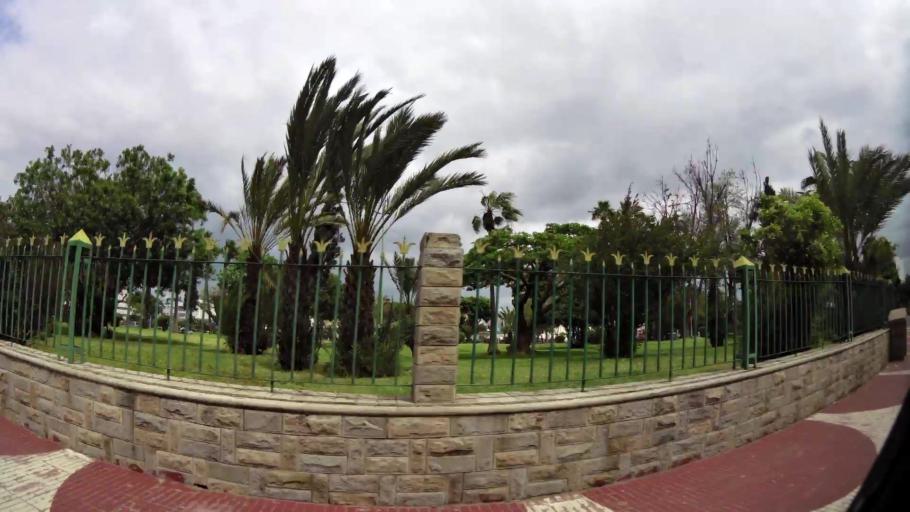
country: MA
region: Grand Casablanca
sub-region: Casablanca
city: Casablanca
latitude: 33.5643
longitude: -7.5555
